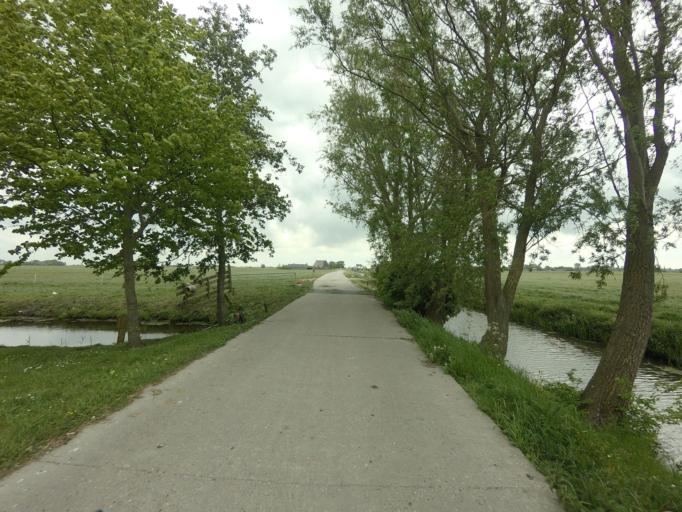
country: NL
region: Friesland
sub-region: Gemeente Littenseradiel
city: Wommels
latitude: 53.1090
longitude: 5.6146
